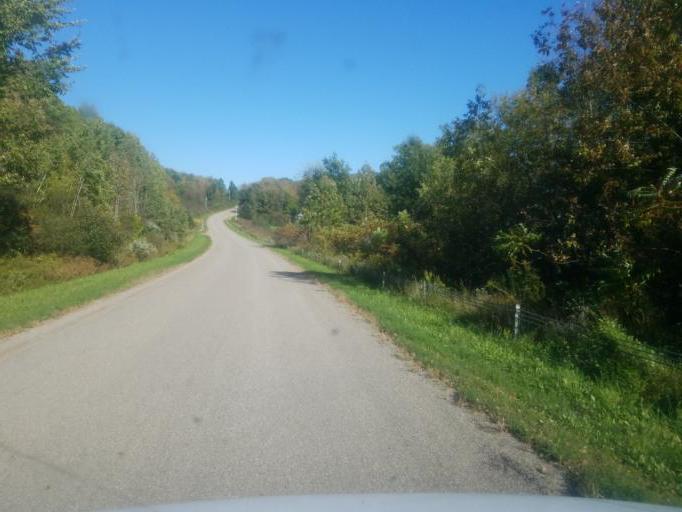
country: US
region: New York
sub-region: Allegany County
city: Cuba
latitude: 42.2272
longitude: -78.2553
